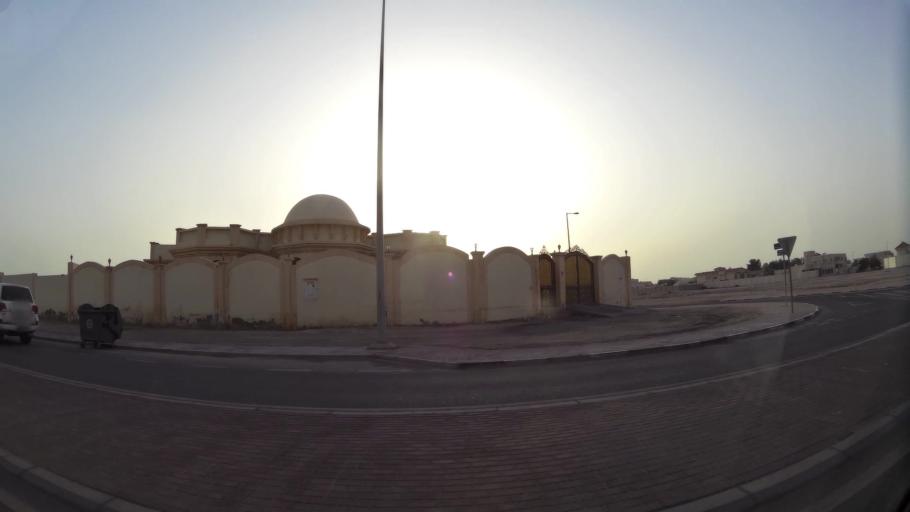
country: QA
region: Baladiyat ar Rayyan
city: Ar Rayyan
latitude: 25.2444
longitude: 51.4442
